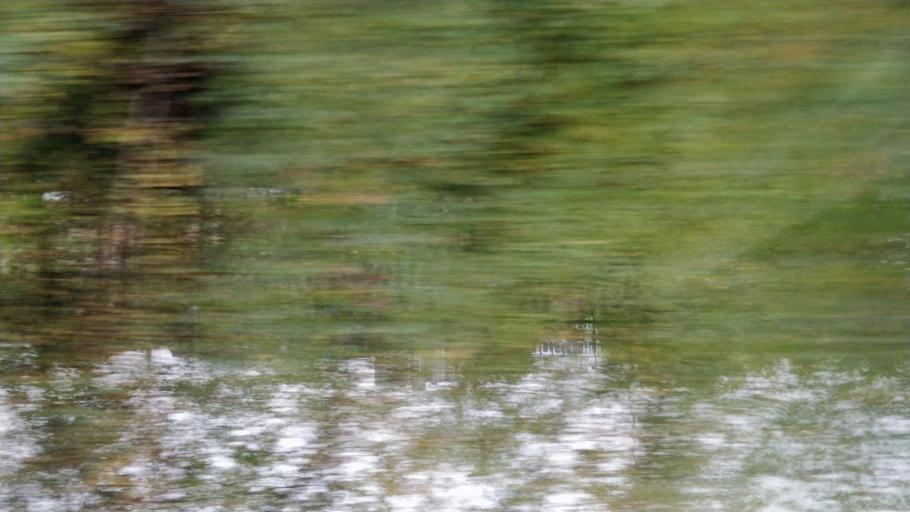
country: GB
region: England
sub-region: Borough of Wigan
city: Ince-in-Makerfield
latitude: 53.5418
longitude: -2.6288
